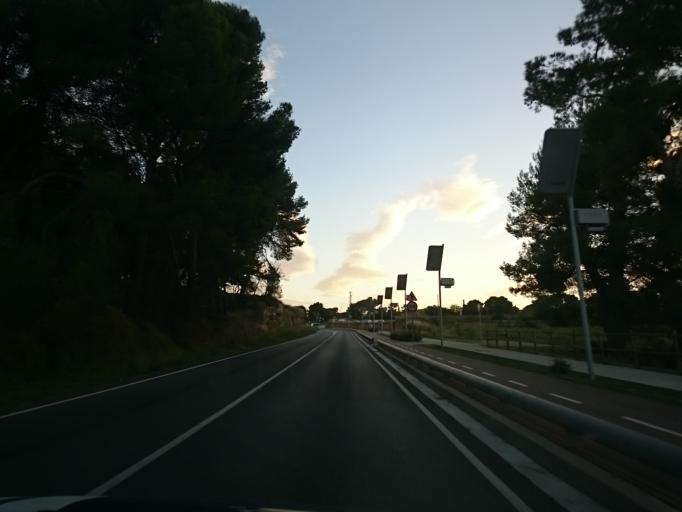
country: ES
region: Catalonia
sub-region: Provincia de Barcelona
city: Sant Pere de Ribes
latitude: 41.2551
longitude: 1.7702
